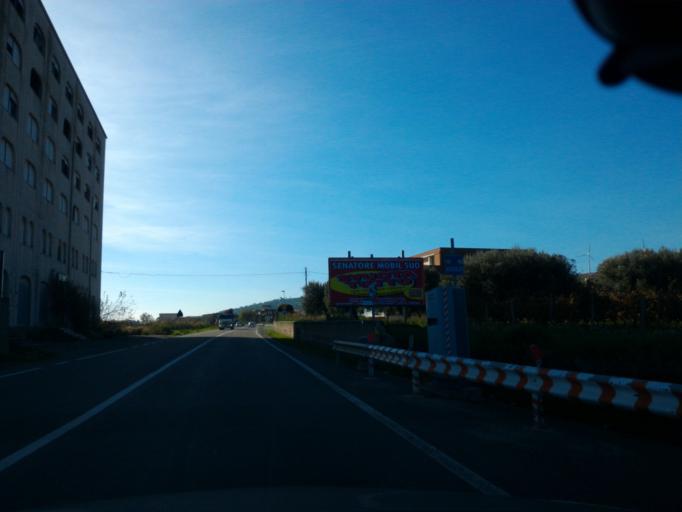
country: IT
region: Calabria
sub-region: Provincia di Crotone
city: Torre Melissa
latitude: 39.3222
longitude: 17.1085
